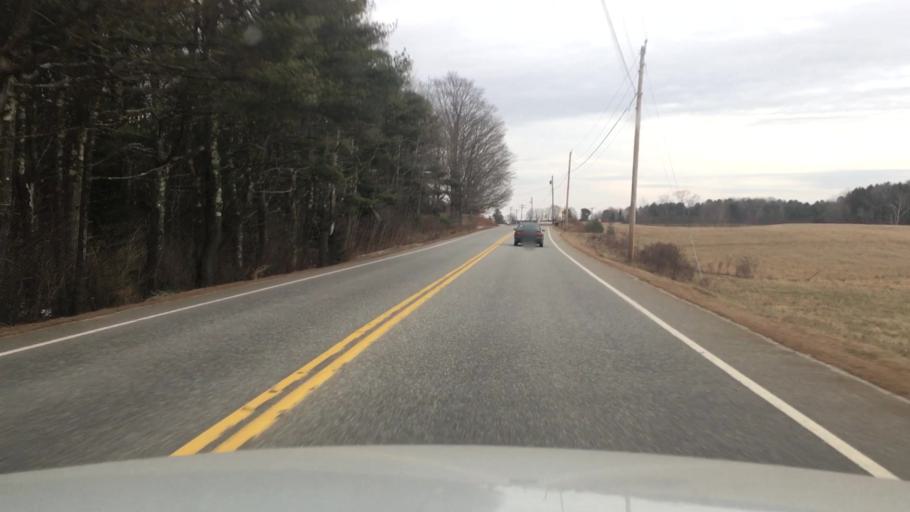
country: US
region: Maine
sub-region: Sagadahoc County
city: Topsham
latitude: 43.8888
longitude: -70.0116
